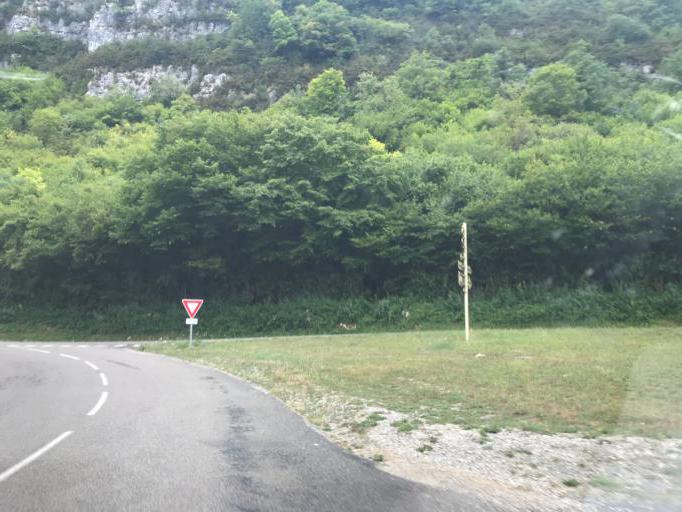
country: FR
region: Rhone-Alpes
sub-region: Departement de l'Ain
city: Dortan
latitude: 46.3494
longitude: 5.6317
